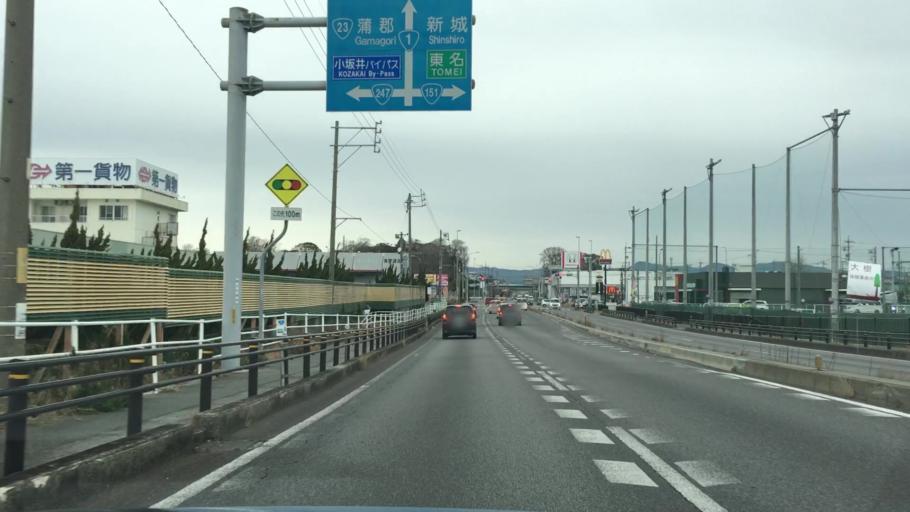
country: JP
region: Aichi
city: Kozakai-cho
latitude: 34.7950
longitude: 137.3690
